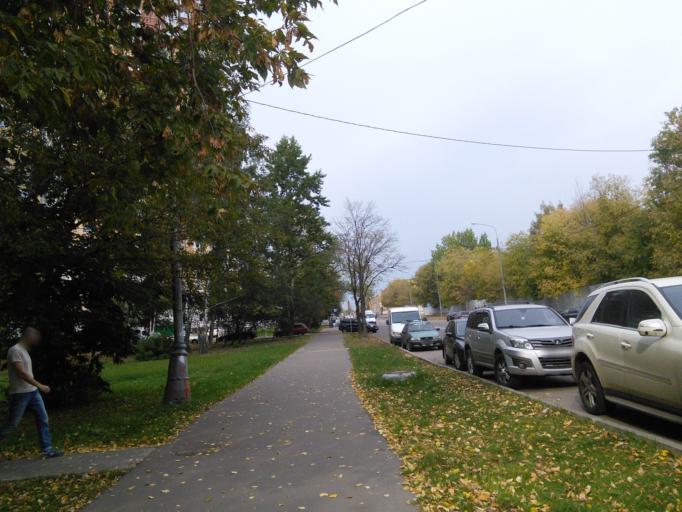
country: RU
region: Moskovskaya
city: Levoberezhnaya
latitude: 55.8682
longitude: 37.4739
